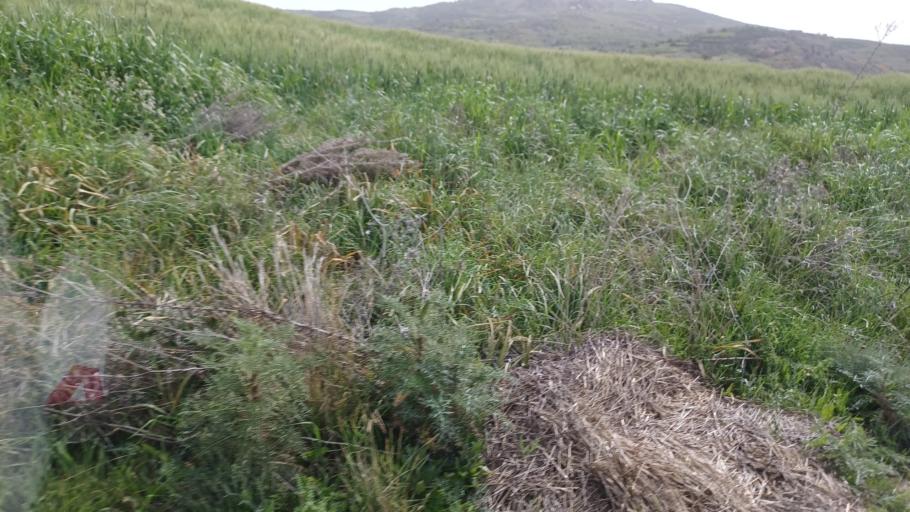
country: CY
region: Pafos
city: Pegeia
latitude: 34.9675
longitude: 32.3539
